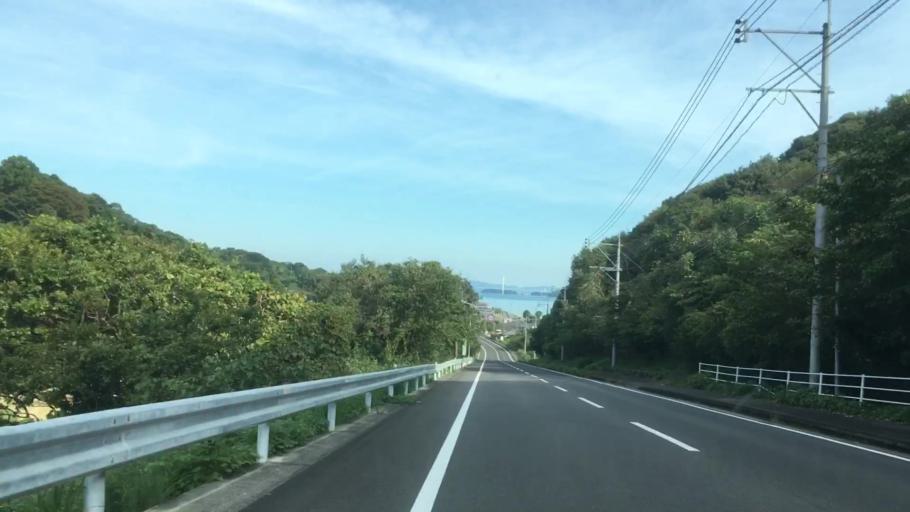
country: JP
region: Nagasaki
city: Sasebo
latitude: 32.9821
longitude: 129.6461
